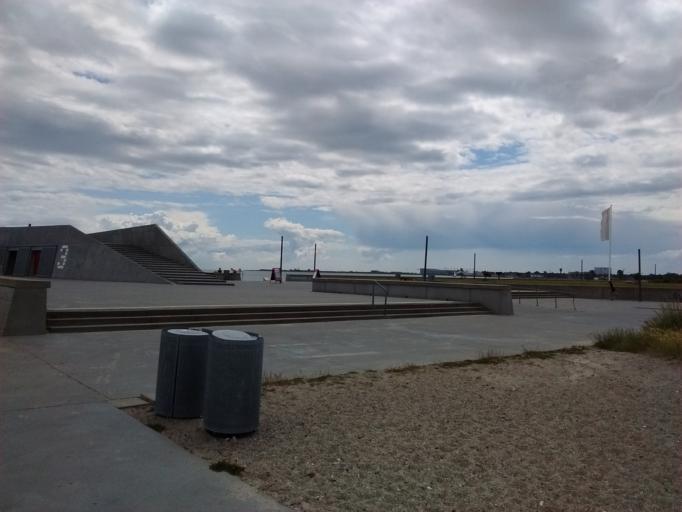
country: DK
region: Capital Region
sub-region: Tarnby Kommune
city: Tarnby
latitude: 55.6549
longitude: 12.6485
